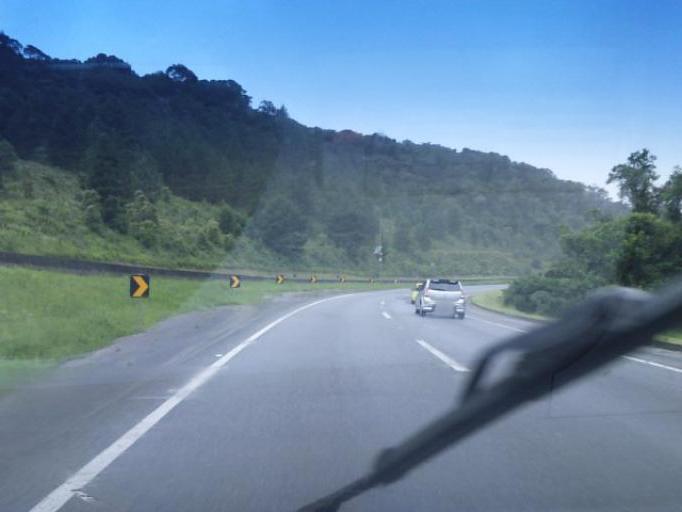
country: BR
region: Parana
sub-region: Antonina
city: Antonina
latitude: -25.0826
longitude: -48.6129
